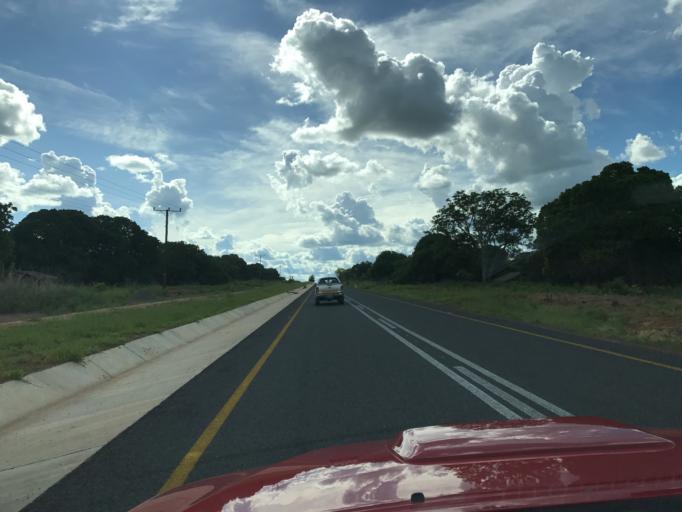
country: MZ
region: Nampula
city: Nampula
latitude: -15.0050
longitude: 38.9863
